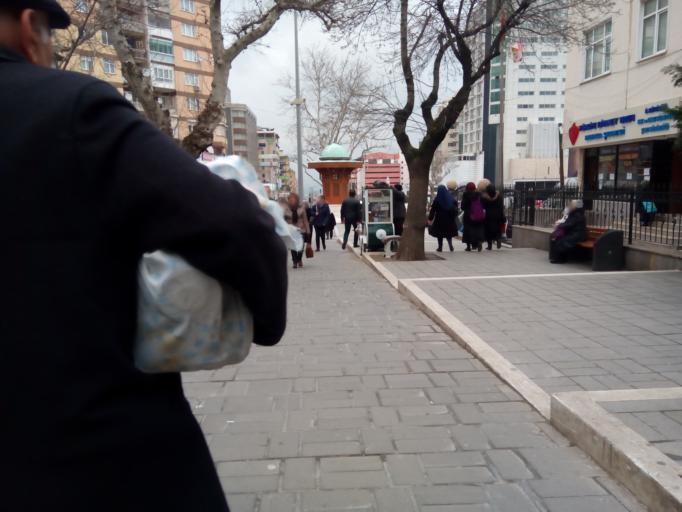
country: TR
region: Bursa
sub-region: Osmangazi
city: Bursa
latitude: 40.1873
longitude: 29.0609
